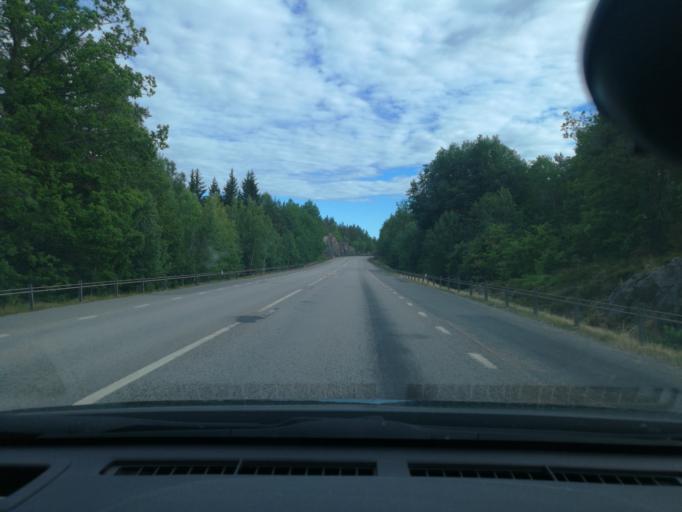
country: SE
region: Kalmar
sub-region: Vasterviks Kommun
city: Ankarsrum
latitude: 57.6505
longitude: 16.4413
